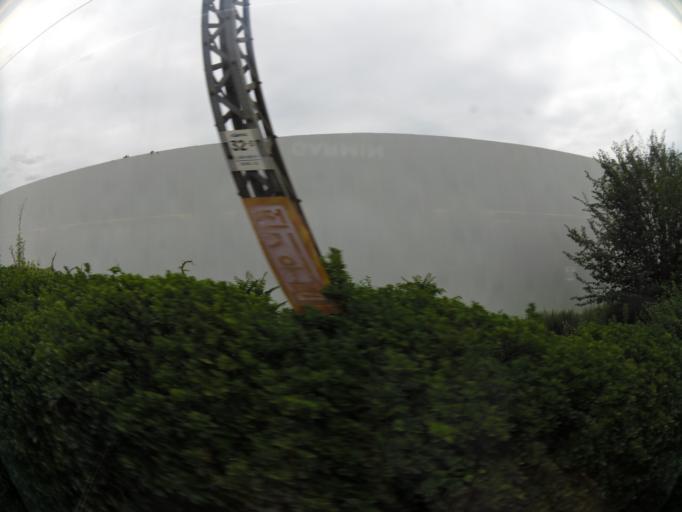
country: KR
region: Seoul
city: Seoul
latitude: 37.5262
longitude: 126.9594
